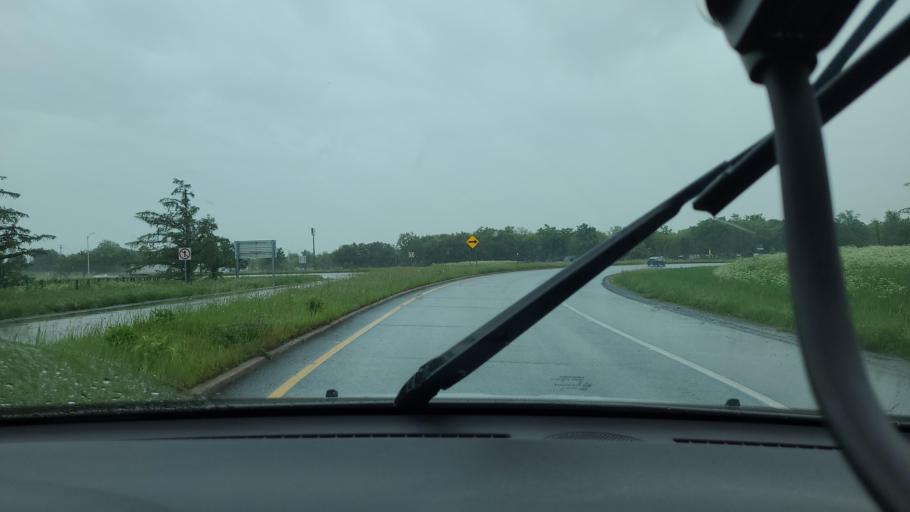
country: CA
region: Quebec
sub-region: Monteregie
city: Beloeil
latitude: 45.6081
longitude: -73.1048
